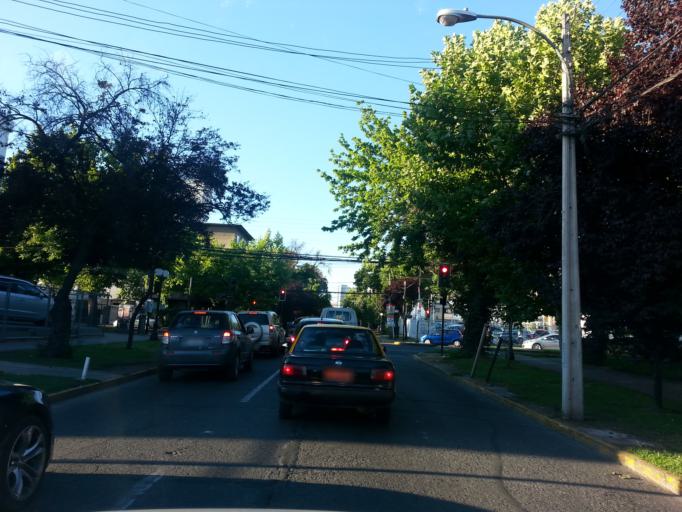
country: CL
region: Santiago Metropolitan
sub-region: Provincia de Santiago
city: Villa Presidente Frei, Nunoa, Santiago, Chile
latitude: -33.4365
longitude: -70.5966
